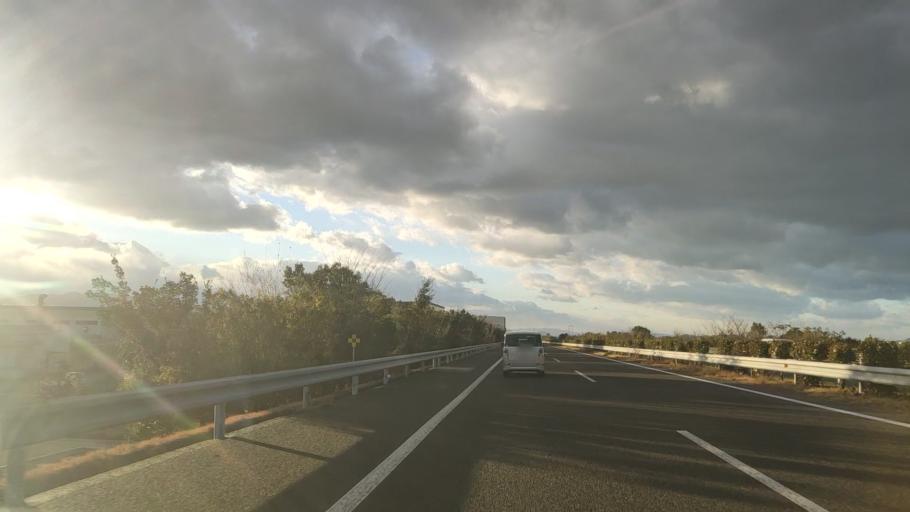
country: JP
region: Ehime
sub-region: Shikoku-chuo Shi
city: Matsuyama
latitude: 33.7858
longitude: 132.8418
